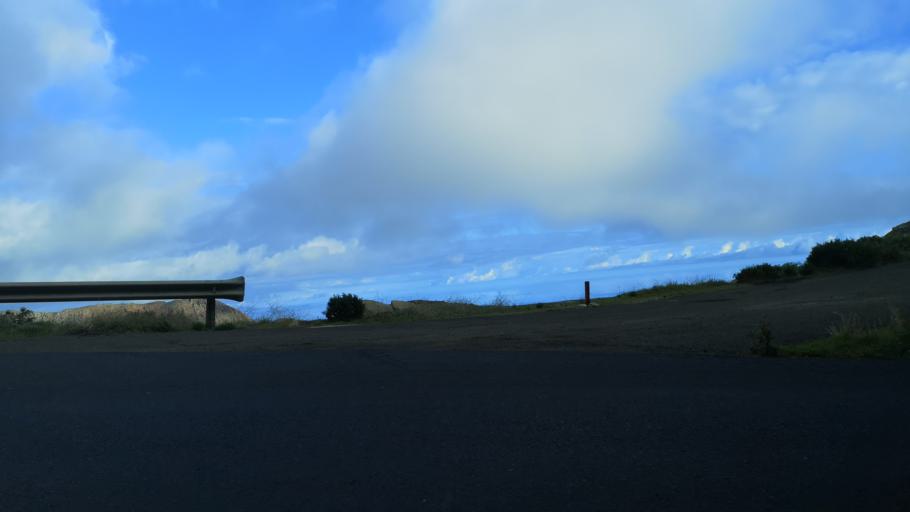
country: ES
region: Canary Islands
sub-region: Provincia de Santa Cruz de Tenerife
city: Alajero
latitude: 28.0819
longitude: -17.1988
